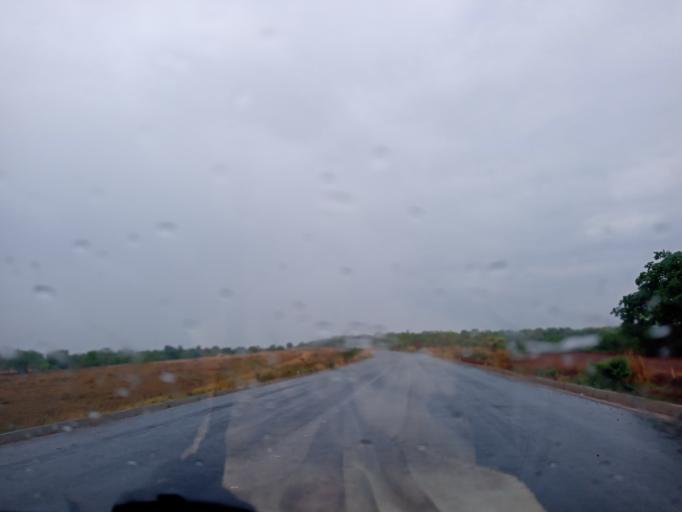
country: BR
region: Minas Gerais
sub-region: Ituiutaba
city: Ituiutaba
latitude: -19.0531
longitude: -49.5050
